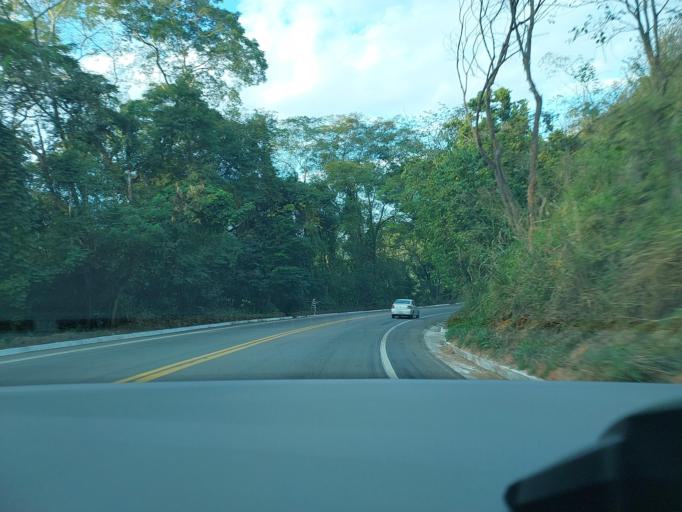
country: BR
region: Minas Gerais
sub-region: Muriae
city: Muriae
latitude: -21.1244
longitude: -42.2816
